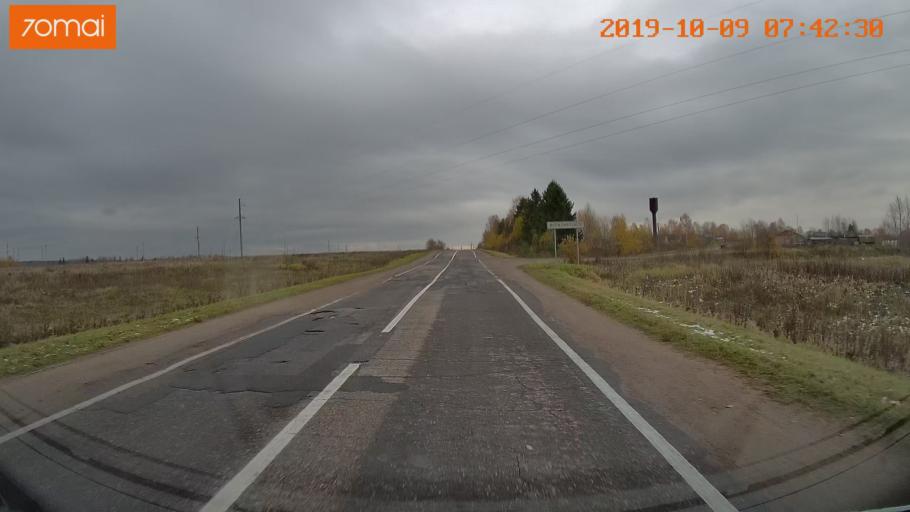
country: RU
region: Jaroslavl
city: Kukoboy
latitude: 58.6431
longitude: 39.7227
